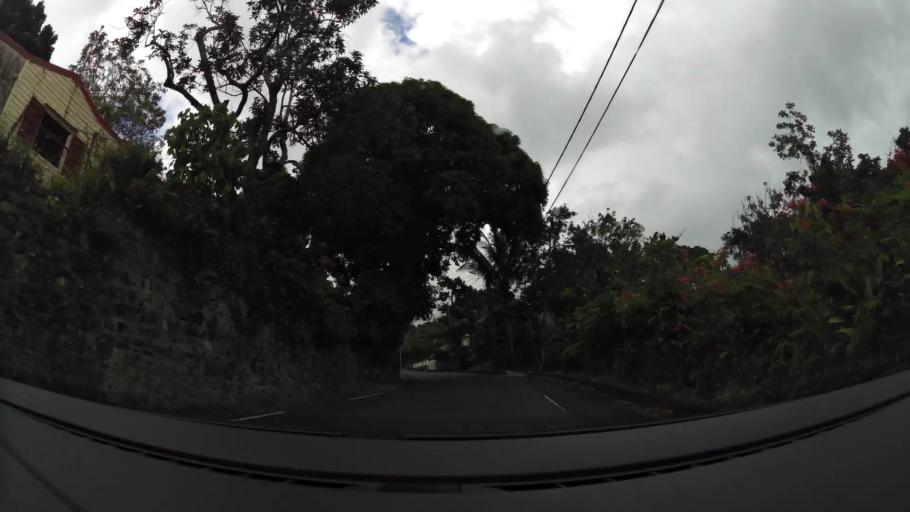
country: GP
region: Guadeloupe
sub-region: Guadeloupe
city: Trois-Rivieres
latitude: 15.9892
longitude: -61.6543
